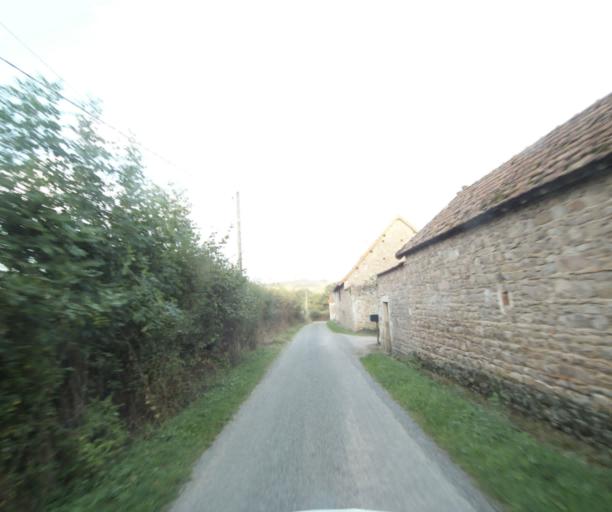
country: FR
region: Bourgogne
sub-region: Departement de Saone-et-Loire
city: Matour
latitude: 46.3940
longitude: 4.4043
